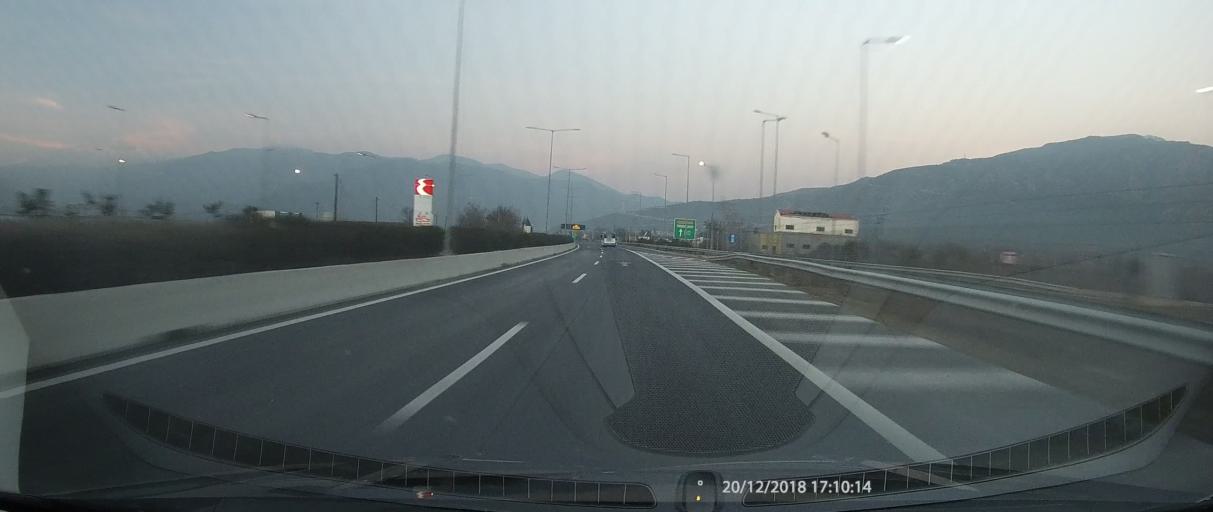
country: GR
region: Thessaly
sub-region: Nomos Larisis
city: Makrychori
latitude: 39.8154
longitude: 22.5082
